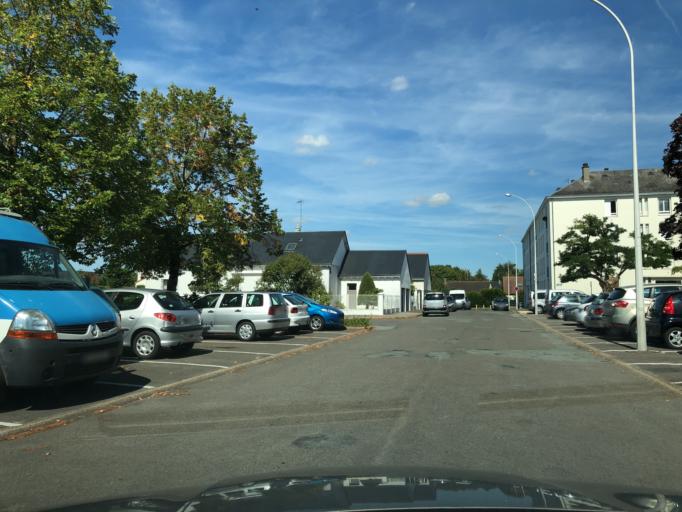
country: FR
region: Centre
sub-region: Departement d'Indre-et-Loire
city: Saint-Cyr-sur-Loire
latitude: 47.4255
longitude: 0.6894
